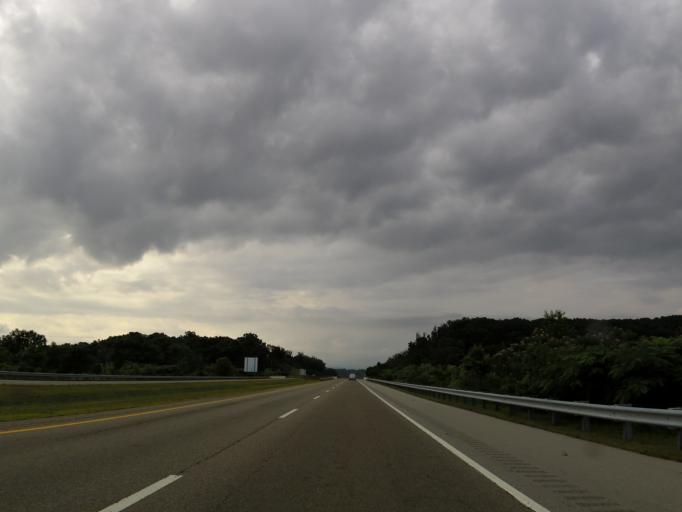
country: US
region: Tennessee
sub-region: Blount County
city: Eagleton Village
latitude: 35.8208
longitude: -83.9530
